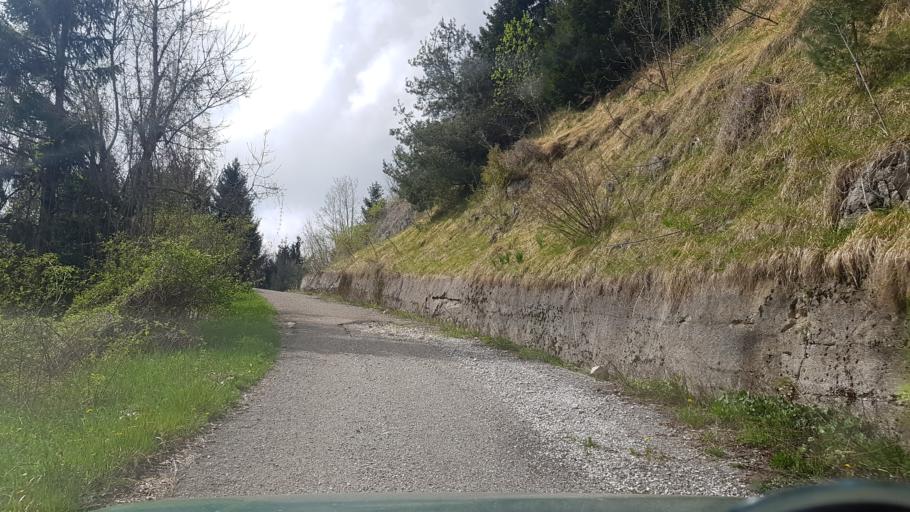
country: IT
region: Friuli Venezia Giulia
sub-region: Provincia di Udine
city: Taipana
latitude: 46.2262
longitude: 13.3540
